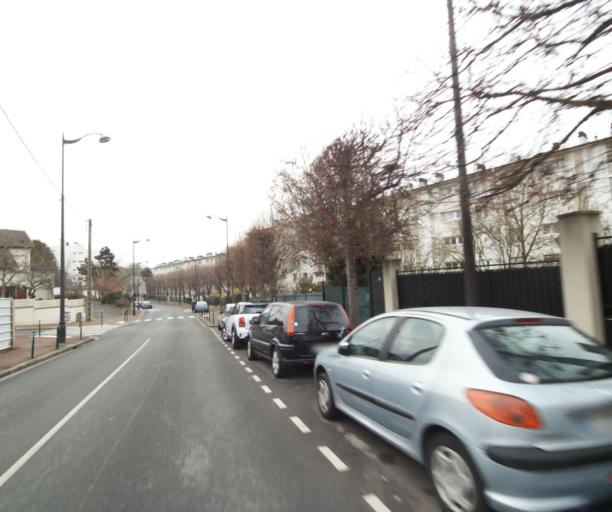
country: FR
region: Ile-de-France
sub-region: Departement des Hauts-de-Seine
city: Rueil-Malmaison
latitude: 48.8691
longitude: 2.1981
